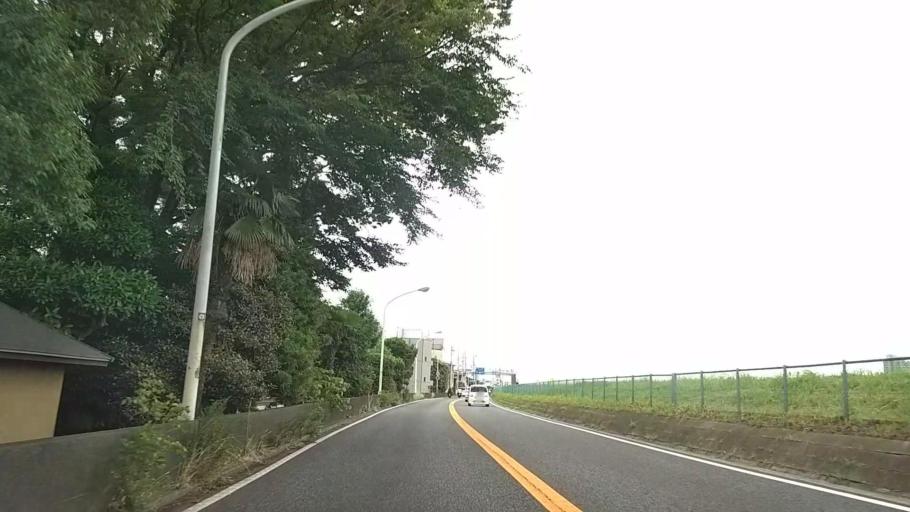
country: JP
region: Kanagawa
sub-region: Kawasaki-shi
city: Kawasaki
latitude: 35.5607
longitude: 139.6793
